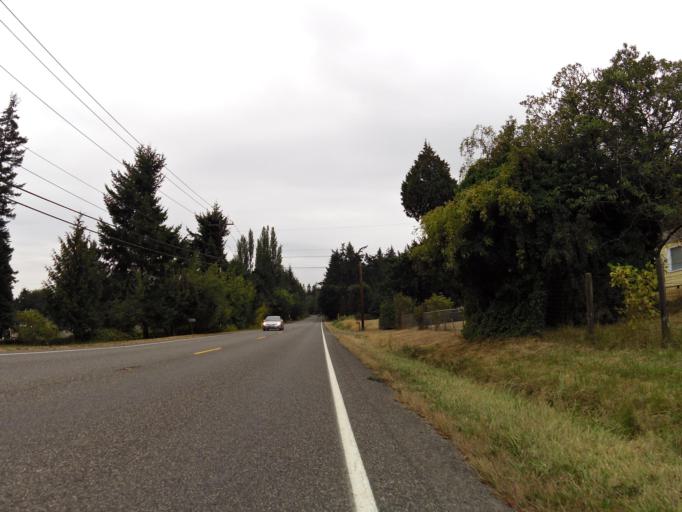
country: US
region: Washington
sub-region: Jefferson County
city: Port Hadlock-Irondale
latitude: 47.9919
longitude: -122.7224
